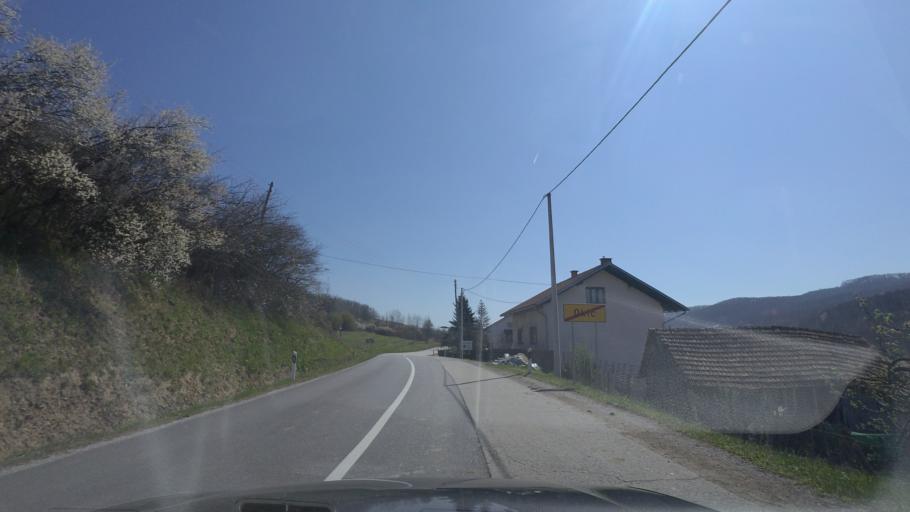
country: HR
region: Karlovacka
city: Vojnic
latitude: 45.3678
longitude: 15.6625
